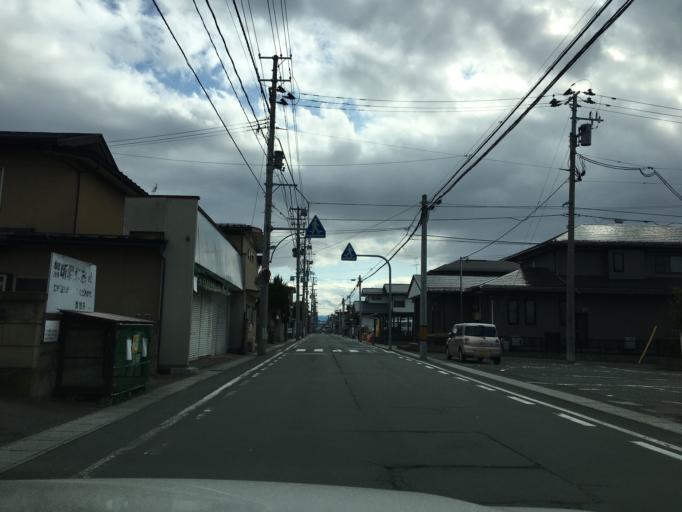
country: JP
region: Yamagata
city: Yamagata-shi
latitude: 38.2585
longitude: 140.3249
